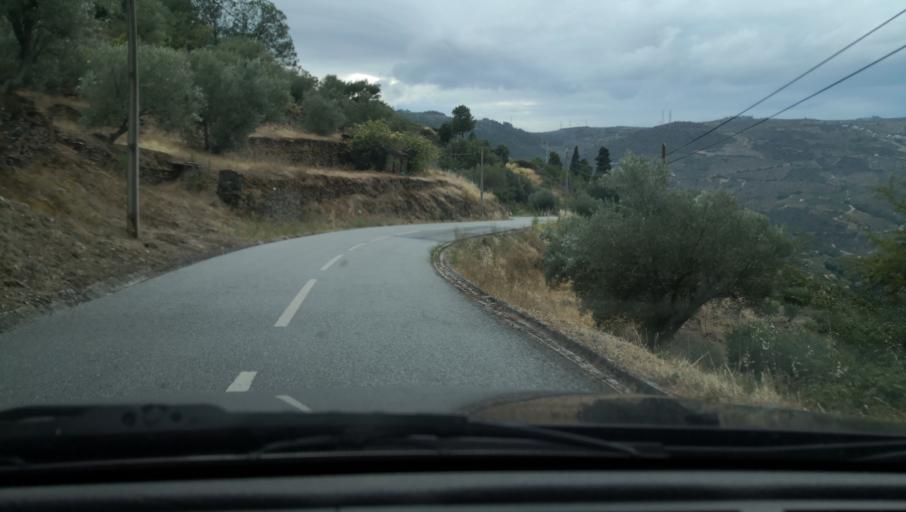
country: PT
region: Viseu
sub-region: Tabuaco
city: Tabuaco
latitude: 41.1276
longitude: -7.6227
